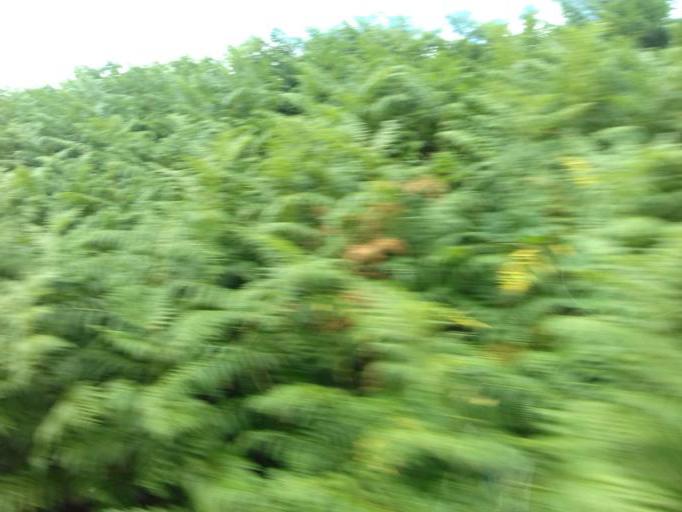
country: IE
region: Leinster
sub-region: County Carlow
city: Bagenalstown
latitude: 52.6279
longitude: -6.8214
